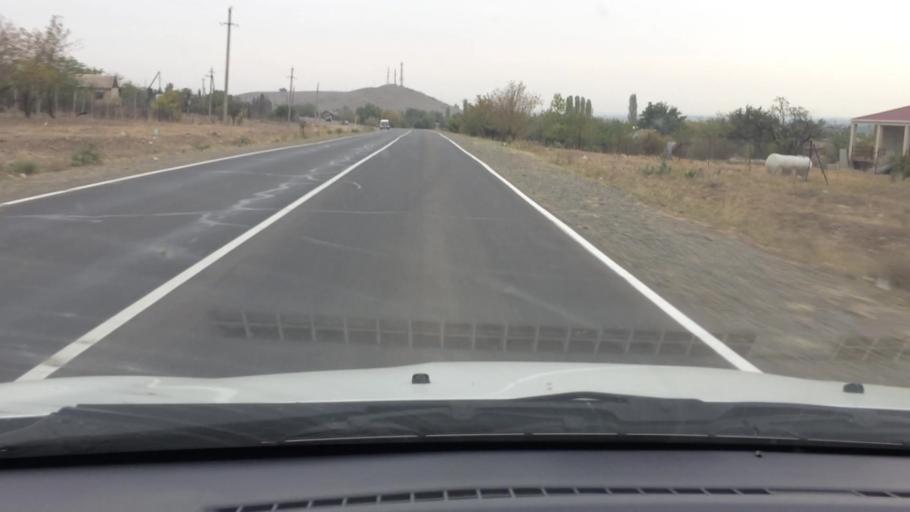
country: GE
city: Naghvarevi
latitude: 41.3557
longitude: 44.8284
